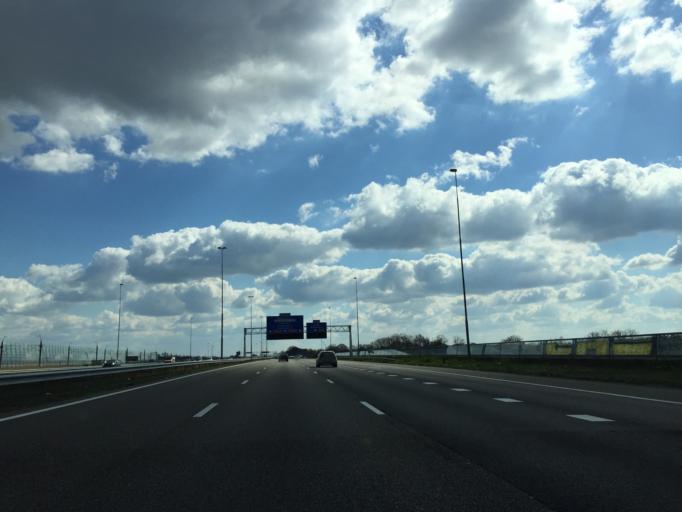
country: NL
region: North Brabant
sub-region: Gemeente Breda
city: Breda
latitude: 51.5692
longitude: 4.7298
